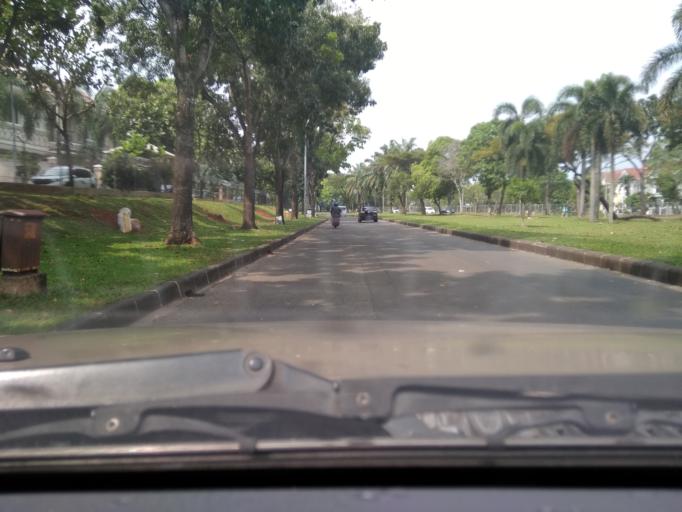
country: ID
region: West Java
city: Serpong
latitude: -6.2990
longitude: 106.6722
